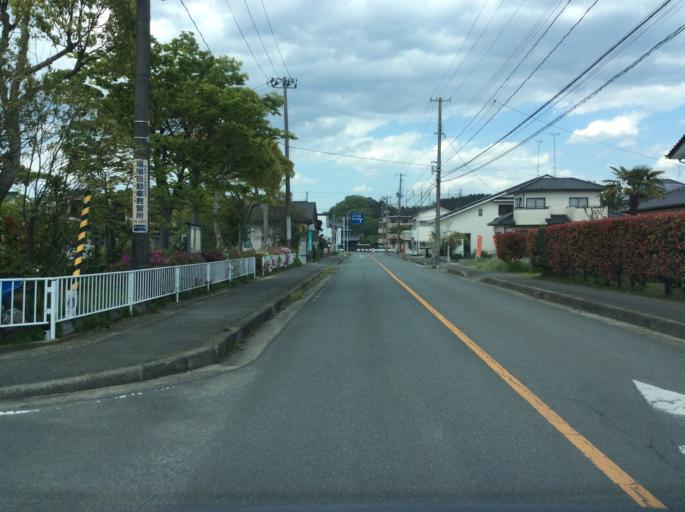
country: JP
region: Ibaraki
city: Kitaibaraki
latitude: 36.8819
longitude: 140.7852
